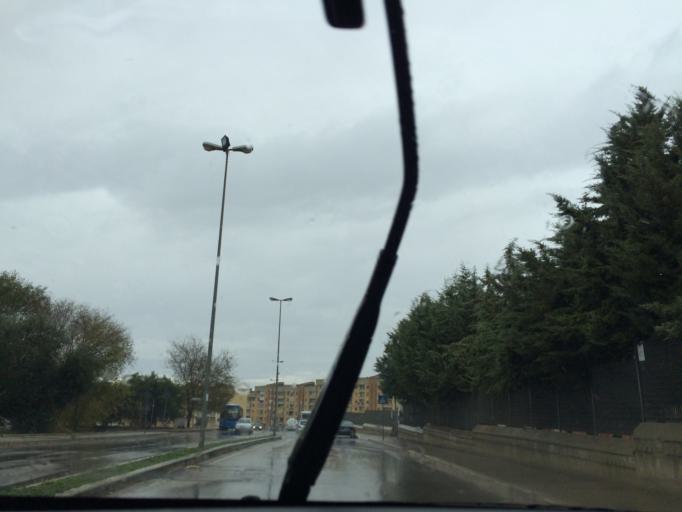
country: IT
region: Basilicate
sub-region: Provincia di Matera
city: Matera
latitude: 40.6792
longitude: 16.5801
